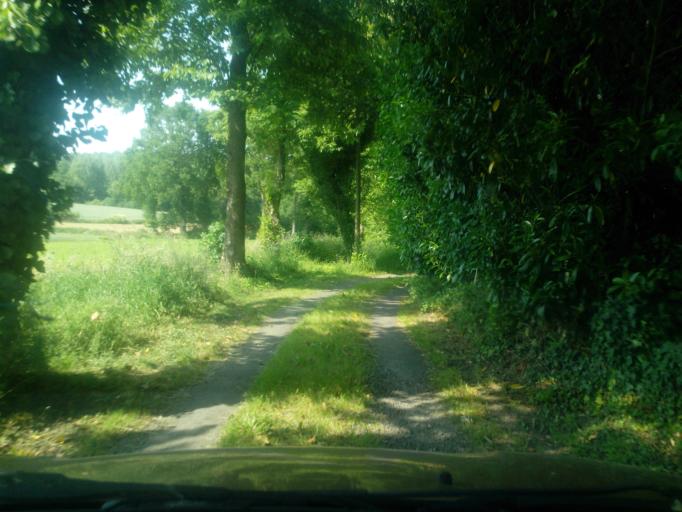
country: FR
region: Brittany
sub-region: Departement d'Ille-et-Vilaine
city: Melesse
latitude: 48.1995
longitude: -1.6799
